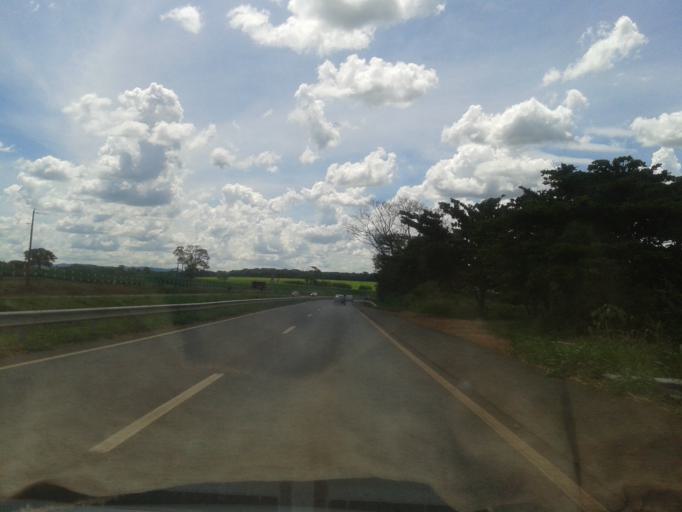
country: BR
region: Goias
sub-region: Itaberai
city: Itaberai
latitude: -16.0218
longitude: -49.8370
